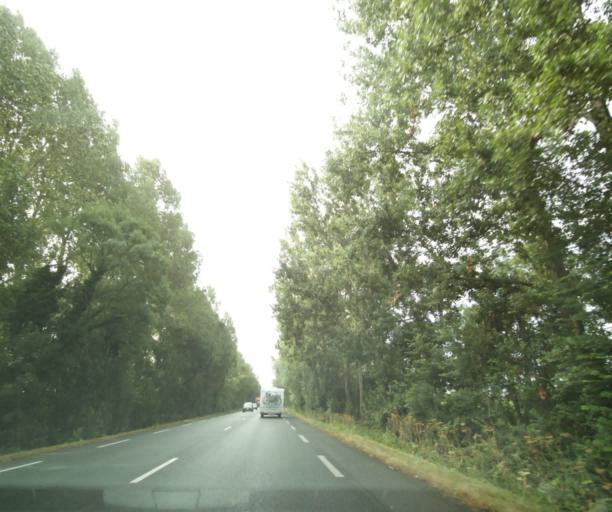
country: FR
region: Pays de la Loire
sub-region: Departement de la Vendee
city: Sainte-Gemme-la-Plaine
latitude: 46.4461
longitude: -1.1024
